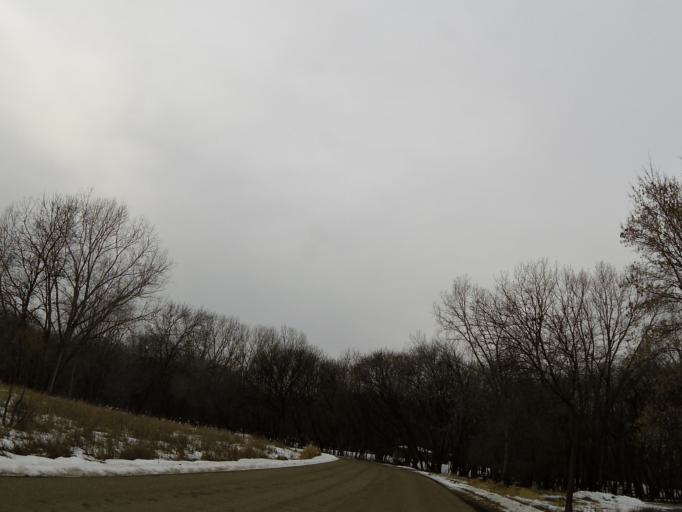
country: US
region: Minnesota
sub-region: Dakota County
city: Mendota Heights
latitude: 44.8862
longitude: -93.1775
